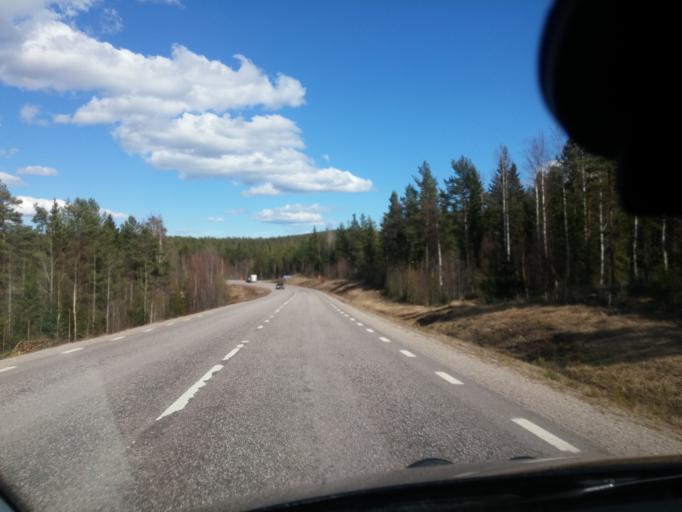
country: SE
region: Gaevleborg
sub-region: Ovanakers Kommun
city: Edsbyn
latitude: 61.2480
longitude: 15.8890
